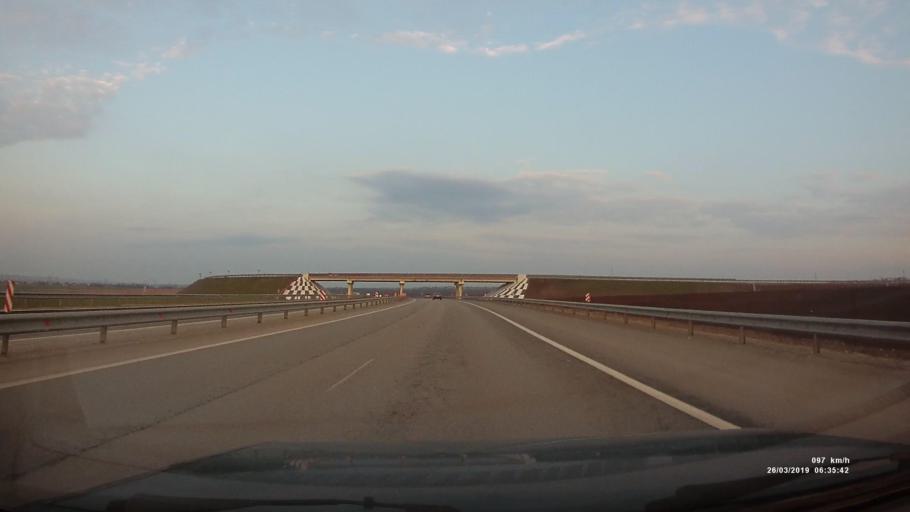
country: RU
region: Rostov
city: Chaltyr
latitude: 47.2828
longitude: 39.4394
